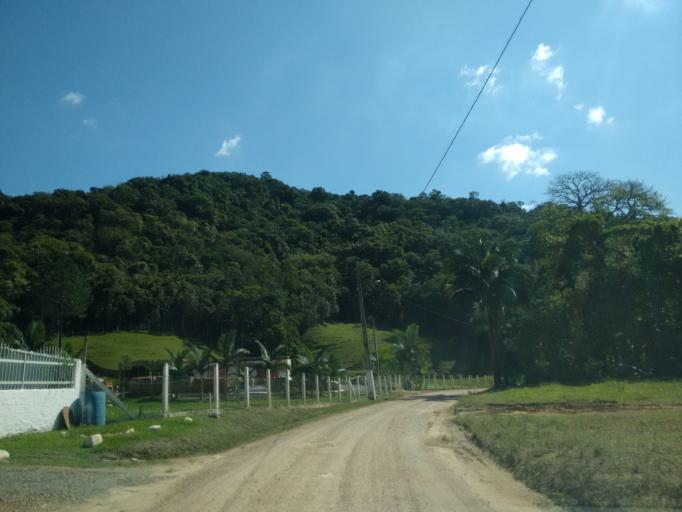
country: BR
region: Santa Catarina
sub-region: Indaial
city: Indaial
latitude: -26.9642
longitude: -49.1789
